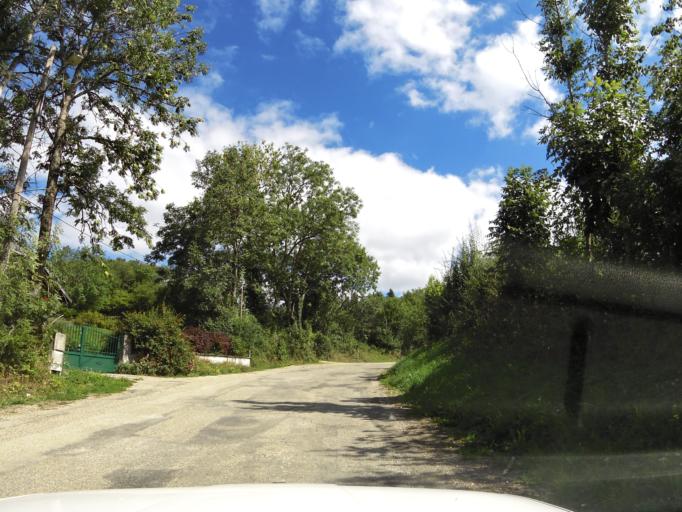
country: FR
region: Rhone-Alpes
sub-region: Departement de l'Ain
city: Hauteville-Lompnes
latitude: 45.9886
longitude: 5.6129
